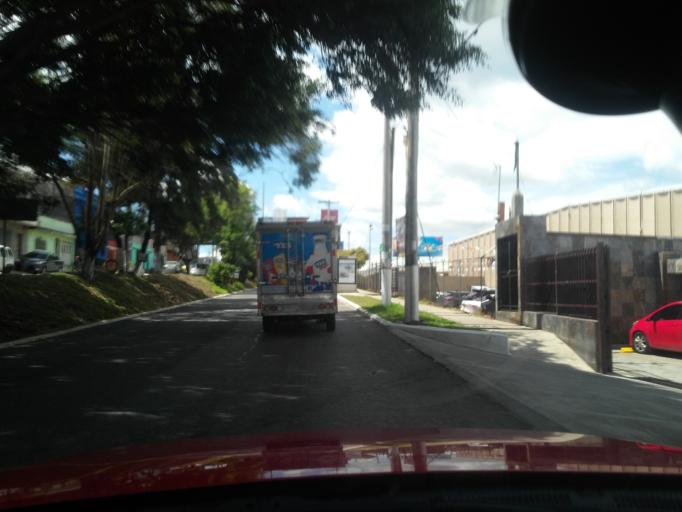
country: GT
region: Guatemala
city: Mixco
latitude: 14.6497
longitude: -90.5678
